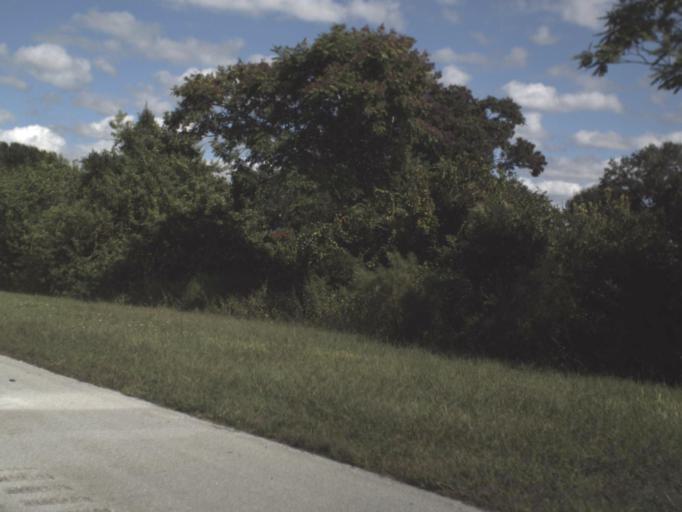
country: US
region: Florida
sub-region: Osceola County
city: Buenaventura Lakes
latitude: 28.2771
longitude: -81.3360
